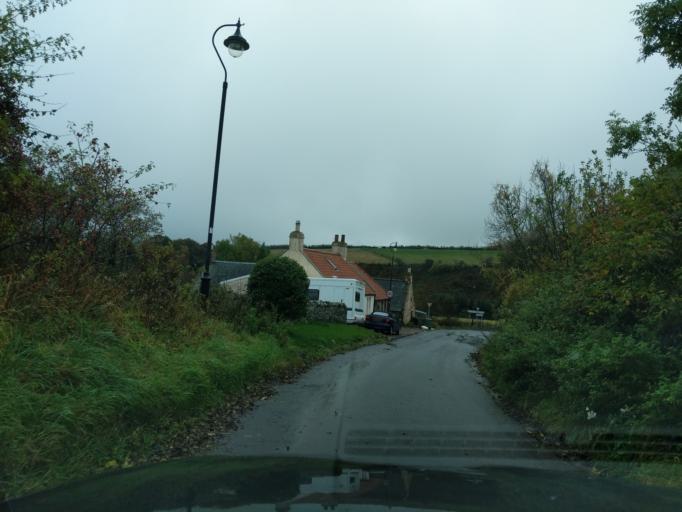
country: GB
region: Scotland
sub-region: East Lothian
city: Dunbar
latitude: 55.9279
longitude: -2.4135
